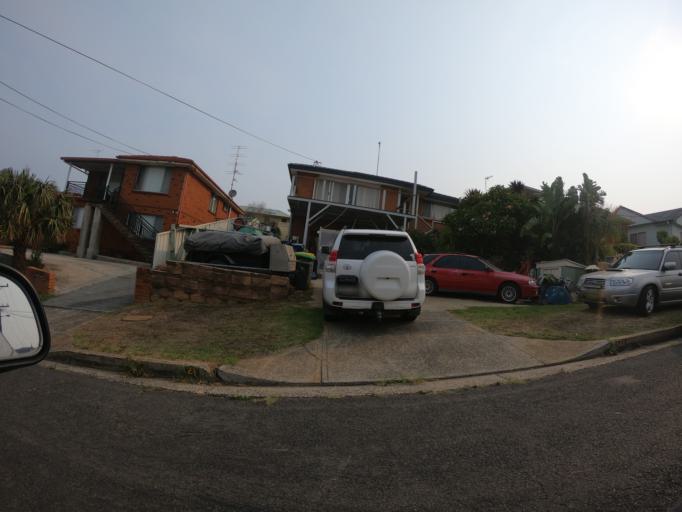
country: AU
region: New South Wales
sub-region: Wollongong
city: Cordeaux Heights
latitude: -34.4528
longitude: 150.8373
